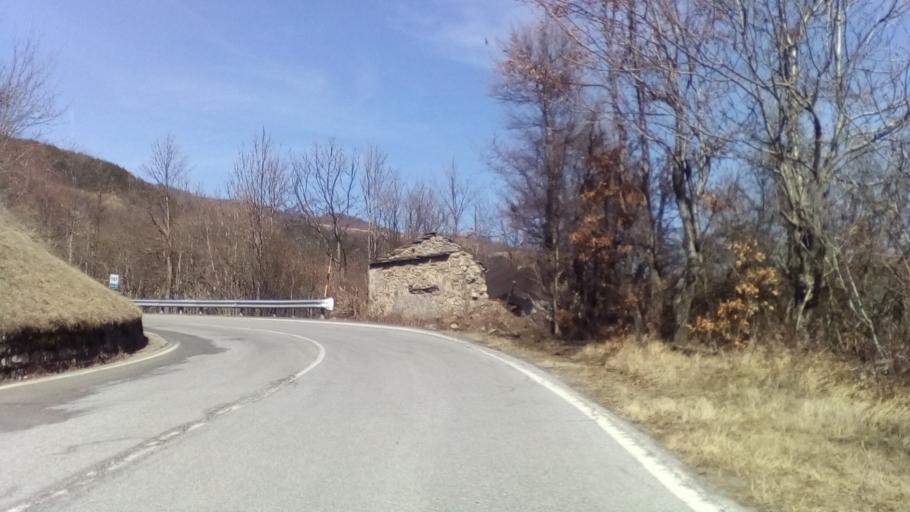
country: IT
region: Emilia-Romagna
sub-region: Provincia di Modena
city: Riolunato
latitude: 44.2315
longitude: 10.6268
